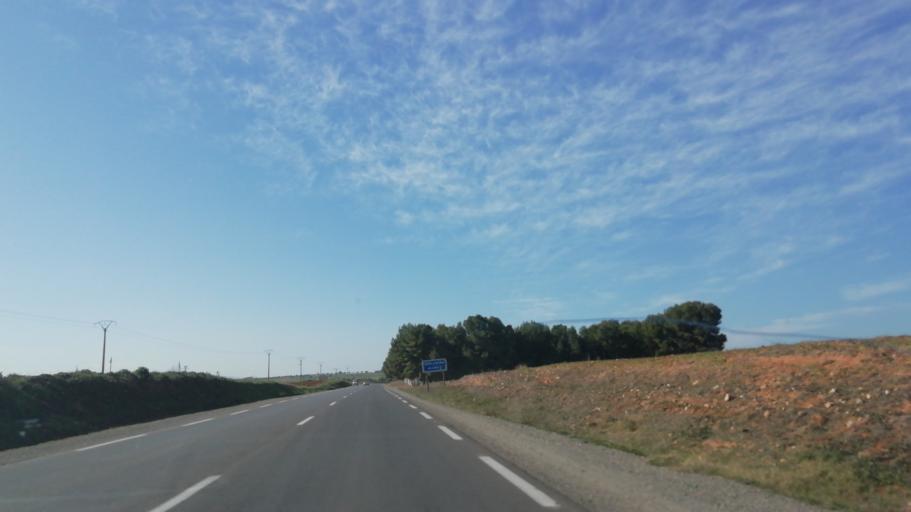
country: DZ
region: Tlemcen
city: Ouled Mimoun
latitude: 35.0318
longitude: -0.8657
